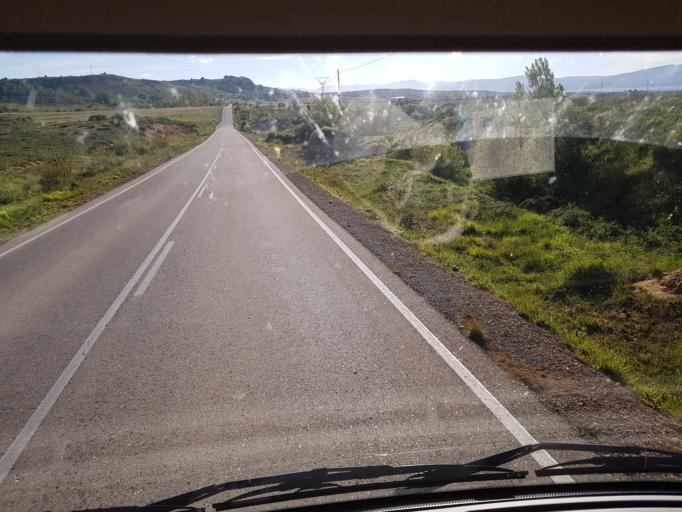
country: ES
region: Castille and Leon
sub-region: Provincia de Burgos
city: Arija
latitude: 42.9770
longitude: -3.8711
